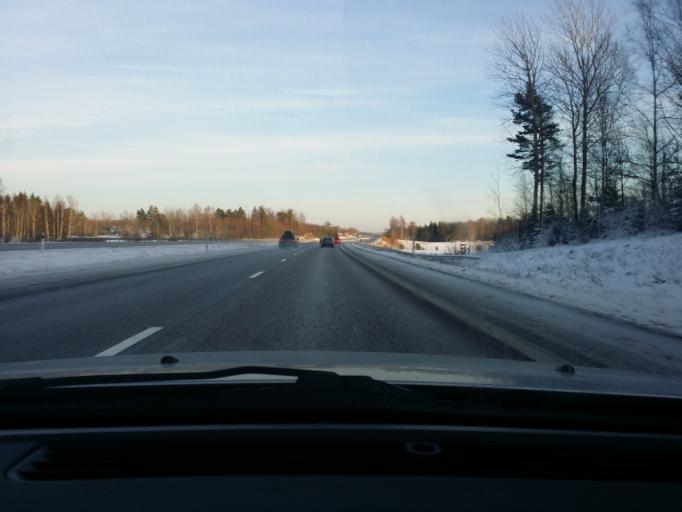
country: SE
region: OErebro
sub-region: Lindesbergs Kommun
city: Fellingsbro
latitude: 59.3226
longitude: 15.4818
